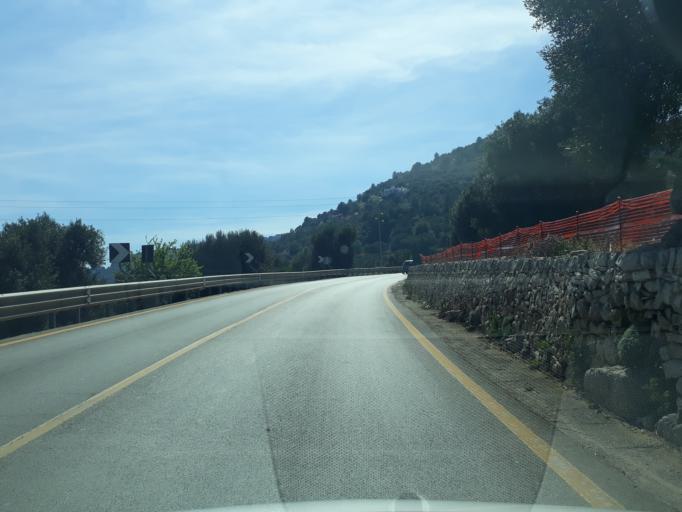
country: IT
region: Apulia
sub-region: Provincia di Brindisi
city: Lamie di Olimpie-Selva
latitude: 40.8186
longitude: 17.3457
